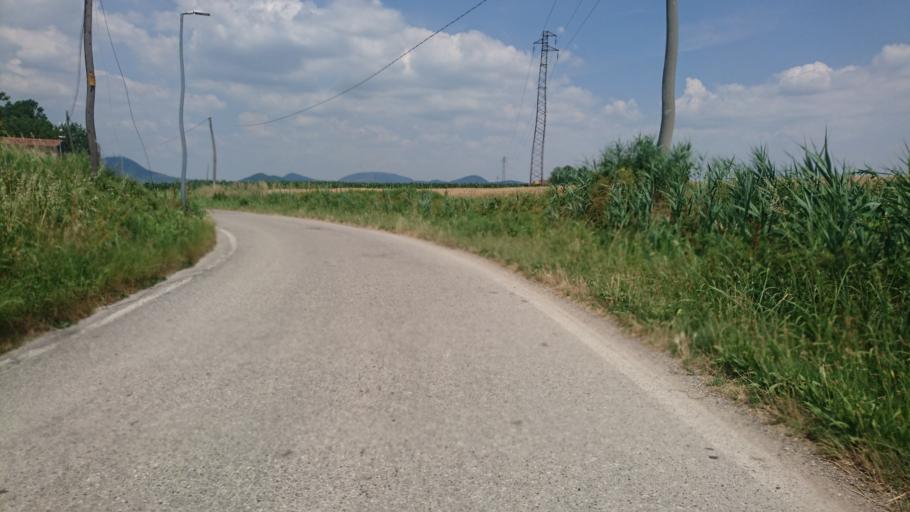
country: IT
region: Veneto
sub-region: Provincia di Padova
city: Sant'Elena
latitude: 45.1979
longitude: 11.7262
